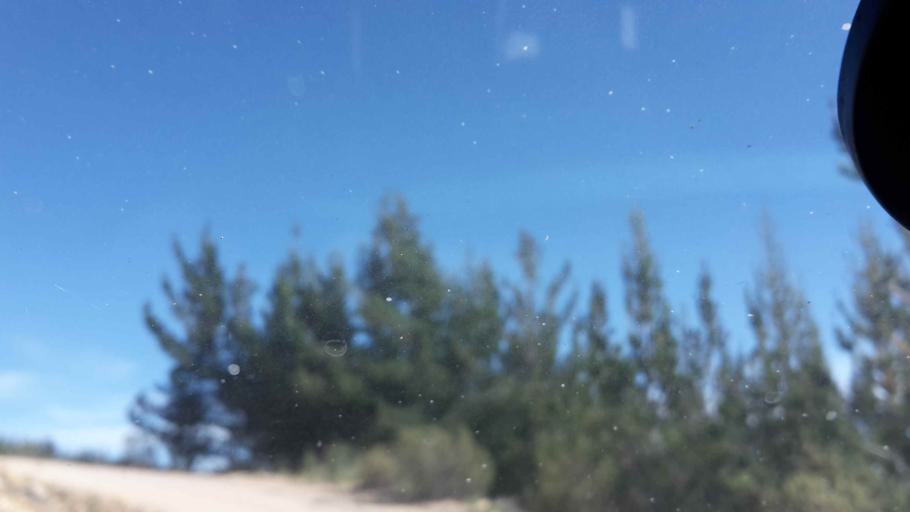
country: BO
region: Cochabamba
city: Arani
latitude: -17.6885
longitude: -65.7210
